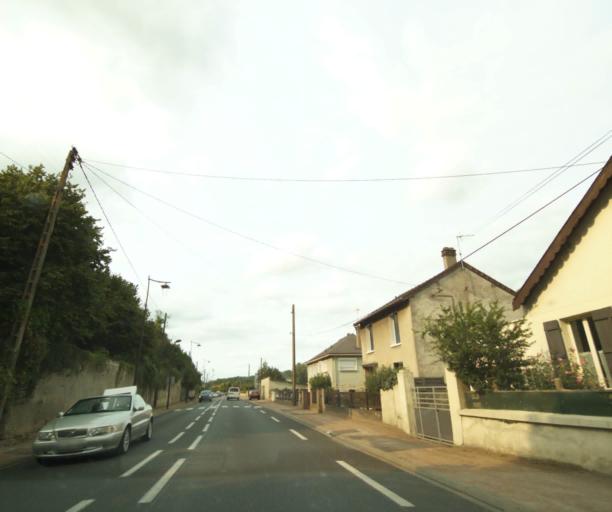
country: FR
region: Centre
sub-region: Departement d'Indre-et-Loire
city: Loches
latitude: 47.1440
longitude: 1.0013
